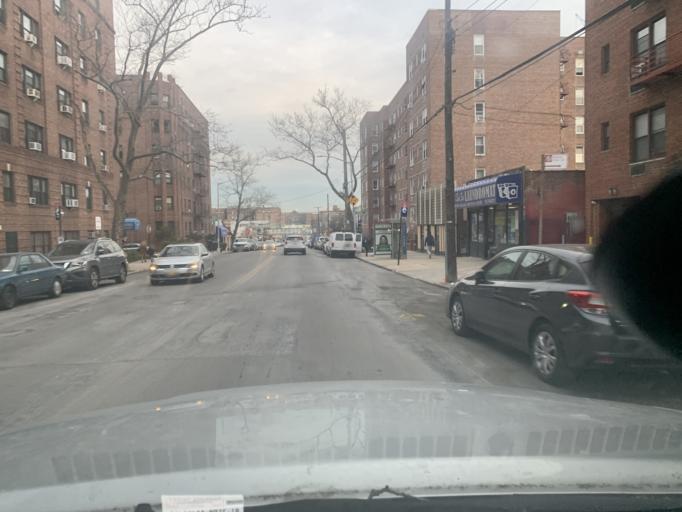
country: US
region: New York
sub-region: Queens County
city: Borough of Queens
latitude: 40.7250
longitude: -73.8656
